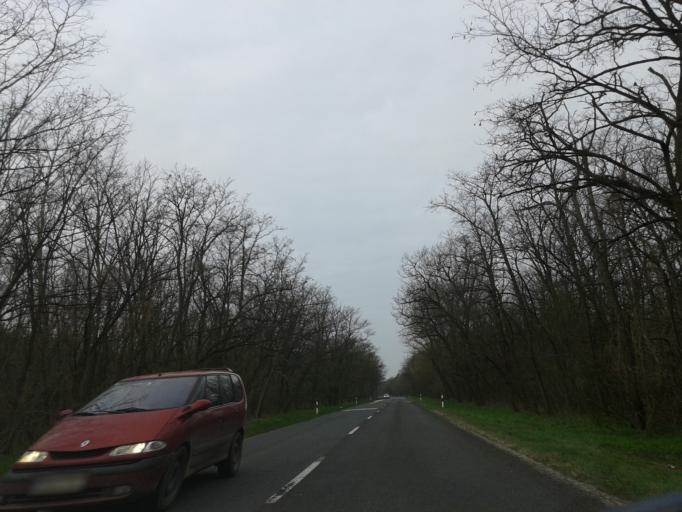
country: HU
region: Komarom-Esztergom
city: Acs
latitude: 47.7394
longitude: 17.9473
